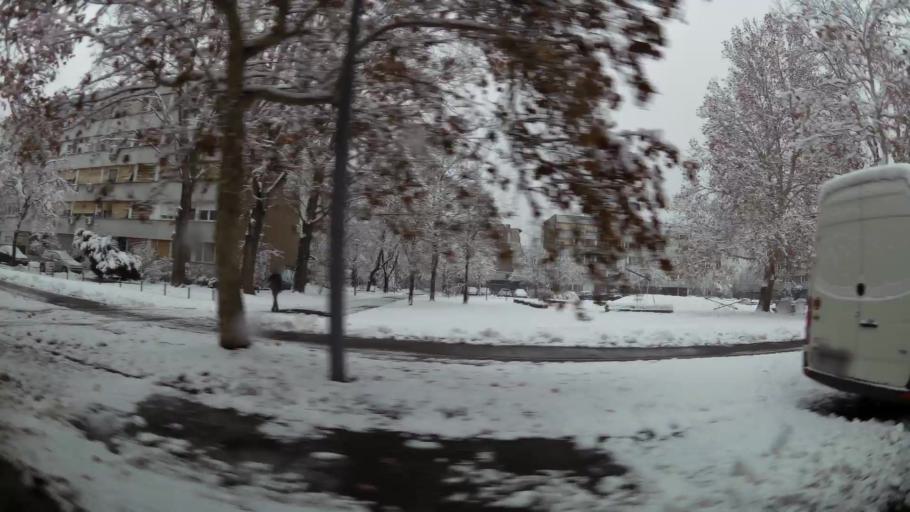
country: RS
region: Central Serbia
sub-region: Belgrade
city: Cukarica
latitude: 44.7988
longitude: 20.3896
